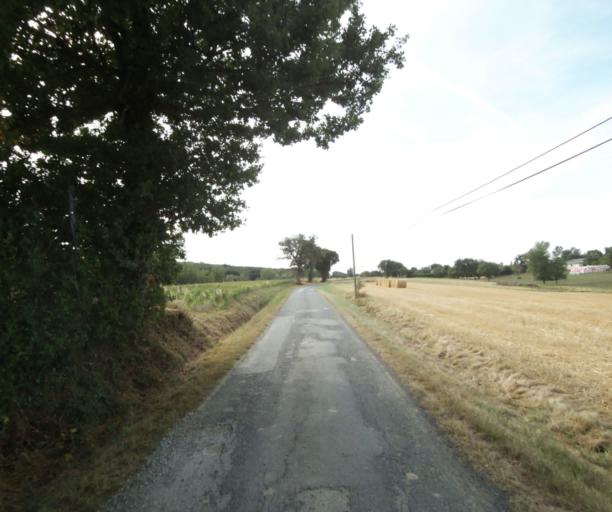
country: FR
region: Midi-Pyrenees
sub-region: Departement du Tarn
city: Puylaurens
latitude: 43.5312
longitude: 2.0570
